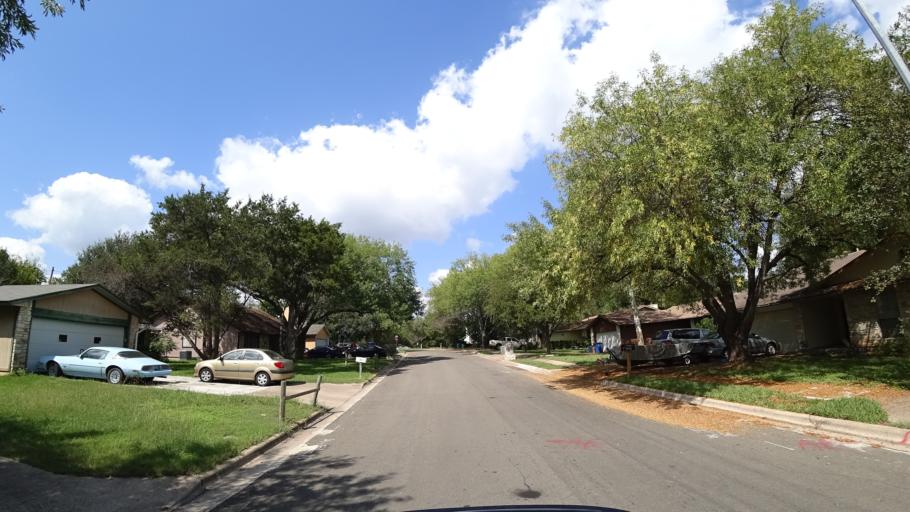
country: US
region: Texas
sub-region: Travis County
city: Onion Creek
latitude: 30.1868
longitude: -97.7898
